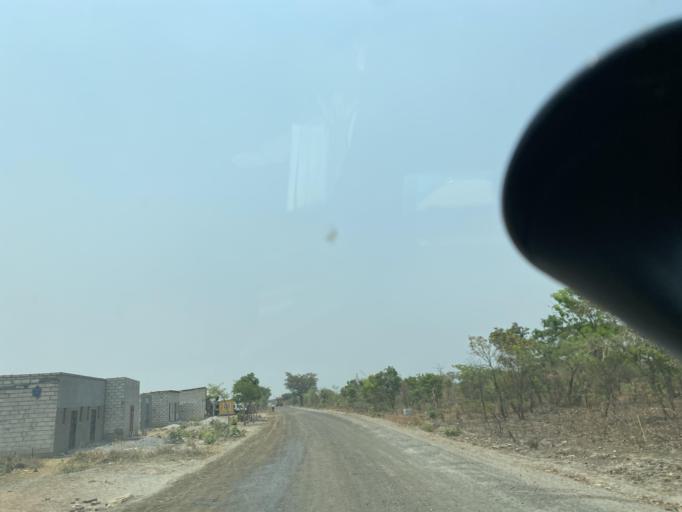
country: ZM
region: Lusaka
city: Lusaka
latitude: -15.5561
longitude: 28.4413
